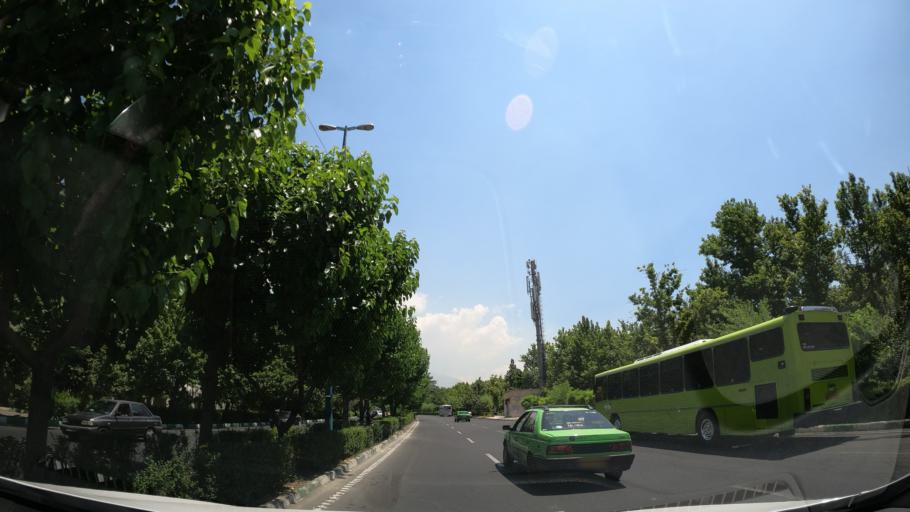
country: IR
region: Tehran
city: Tajrish
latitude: 35.7576
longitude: 51.3731
